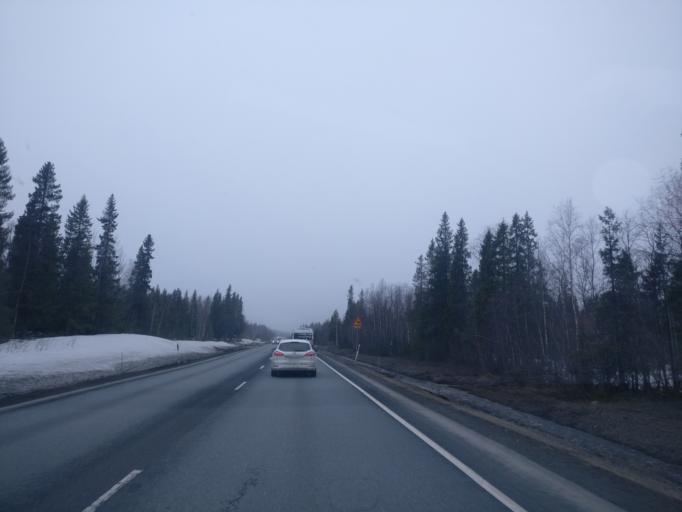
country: FI
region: Lapland
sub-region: Kemi-Tornio
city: Simo
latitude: 65.6748
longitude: 24.8868
